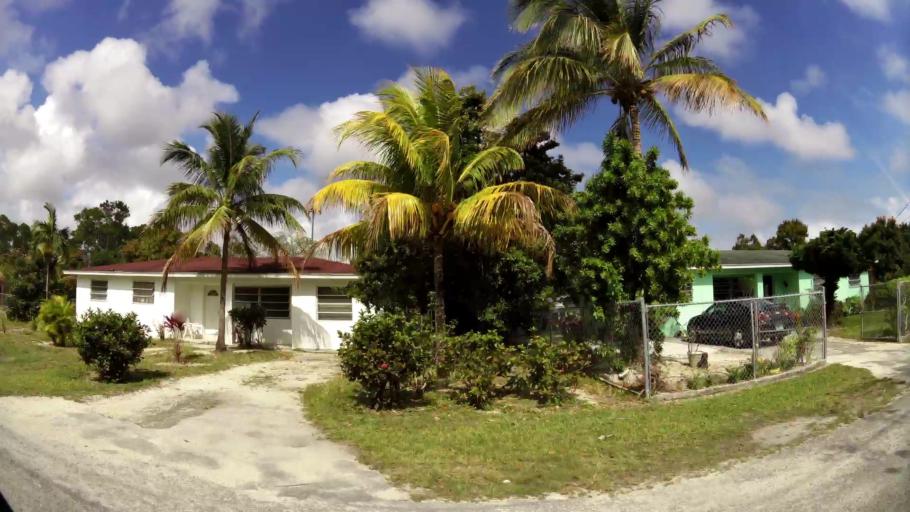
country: BS
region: Freeport
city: Lucaya
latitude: 26.5319
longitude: -78.6760
